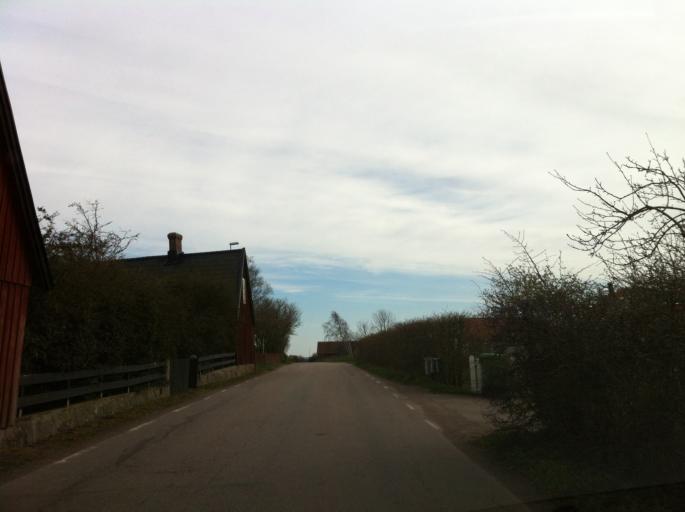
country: SE
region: Skane
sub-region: Hoganas Kommun
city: Hoganas
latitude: 56.2657
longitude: 12.5800
